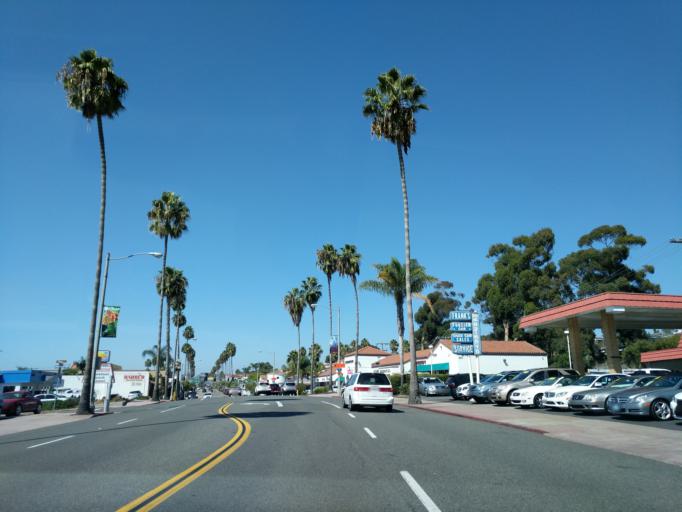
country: US
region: California
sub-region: Orange County
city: San Clemente
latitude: 33.4250
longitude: -117.6103
